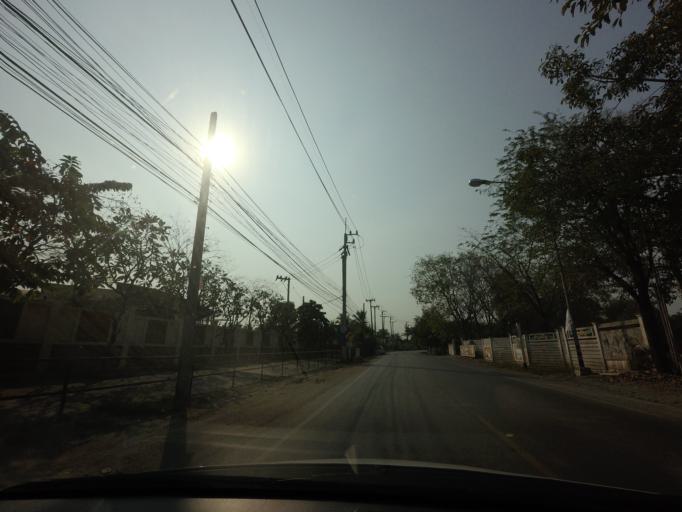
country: TH
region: Nakhon Pathom
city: Sam Phran
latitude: 13.6953
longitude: 100.2308
